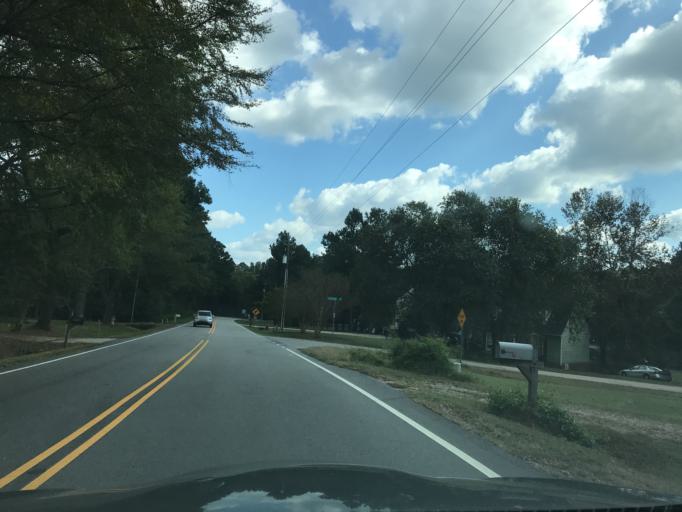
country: US
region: North Carolina
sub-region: Wake County
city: Wake Forest
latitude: 35.9343
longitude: -78.5317
